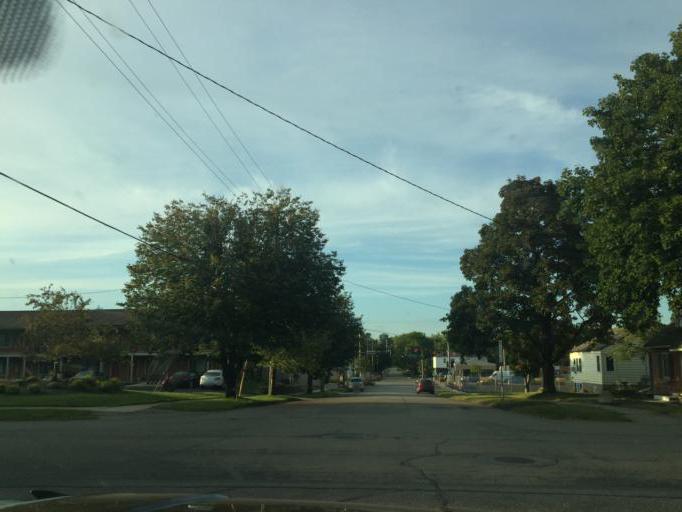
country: US
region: Minnesota
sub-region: Olmsted County
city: Rochester
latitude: 44.0205
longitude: -92.4921
